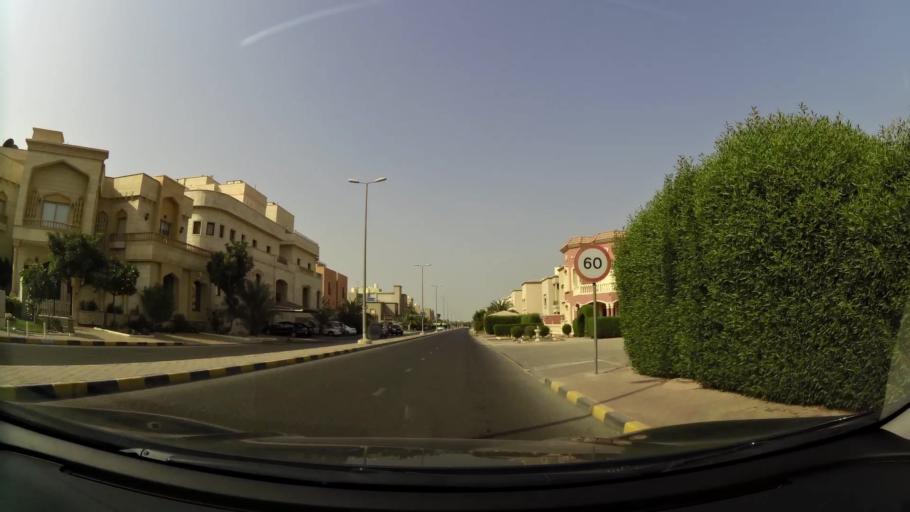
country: KW
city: Bayan
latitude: 29.2847
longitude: 48.0484
